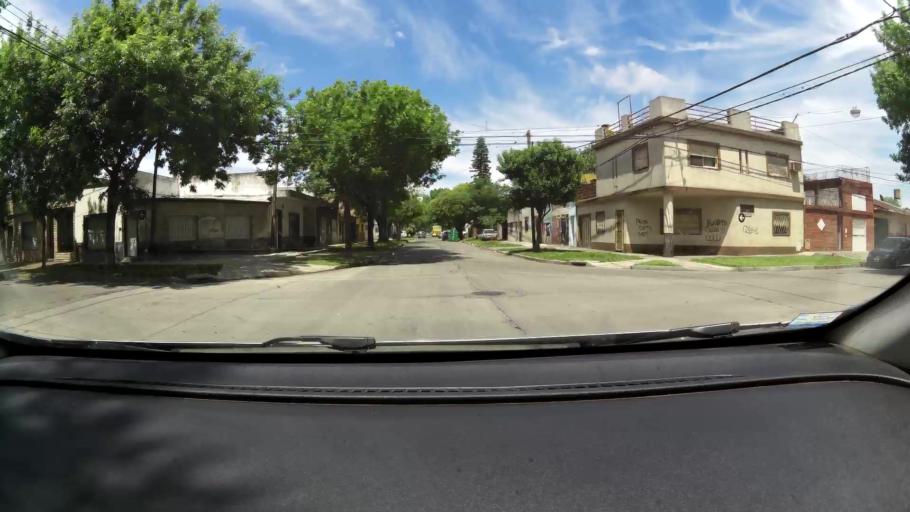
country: AR
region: Santa Fe
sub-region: Departamento de Rosario
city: Rosario
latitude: -32.9773
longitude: -60.6299
